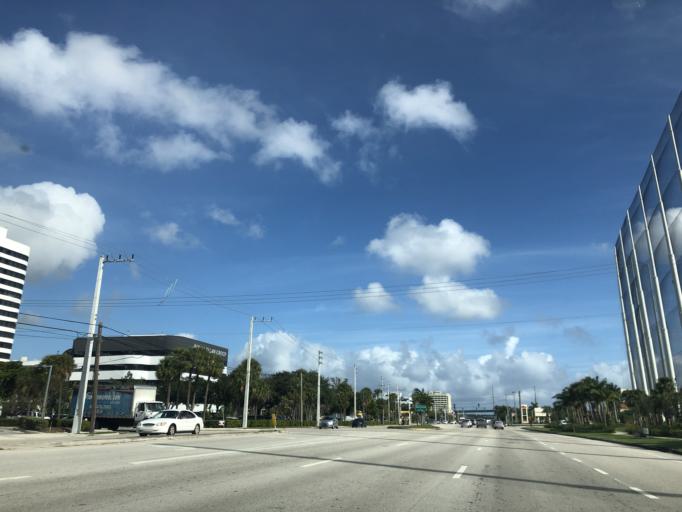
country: US
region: Florida
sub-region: Palm Beach County
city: West Palm Beach
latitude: 26.6909
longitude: -80.0774
